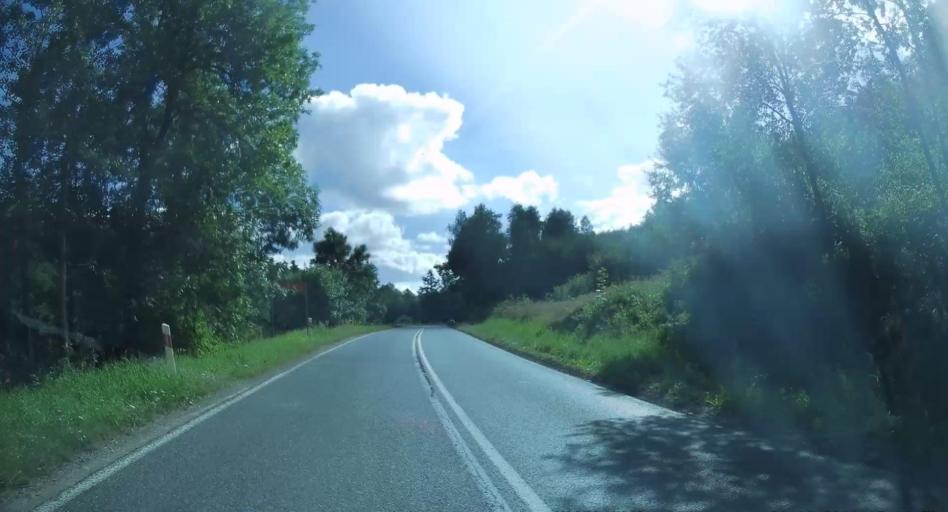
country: PL
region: Swietokrzyskie
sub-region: Powiat kielecki
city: Nowa Slupia
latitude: 50.8328
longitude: 21.0877
